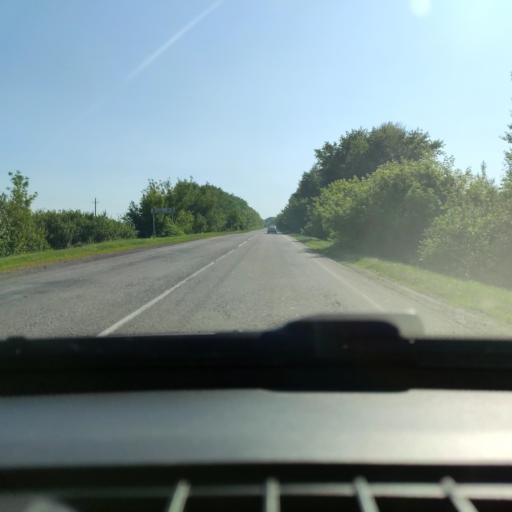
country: RU
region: Voronezj
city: Panino
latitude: 51.6246
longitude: 40.0354
